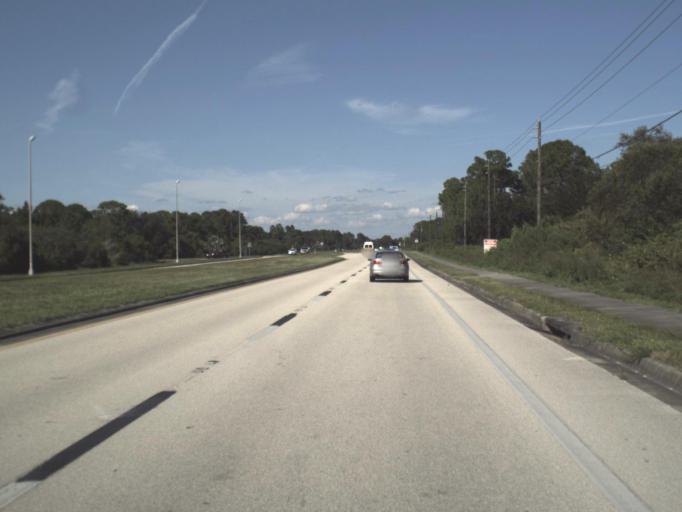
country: US
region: Florida
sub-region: Sarasota County
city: North Port
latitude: 26.9823
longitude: -82.2068
